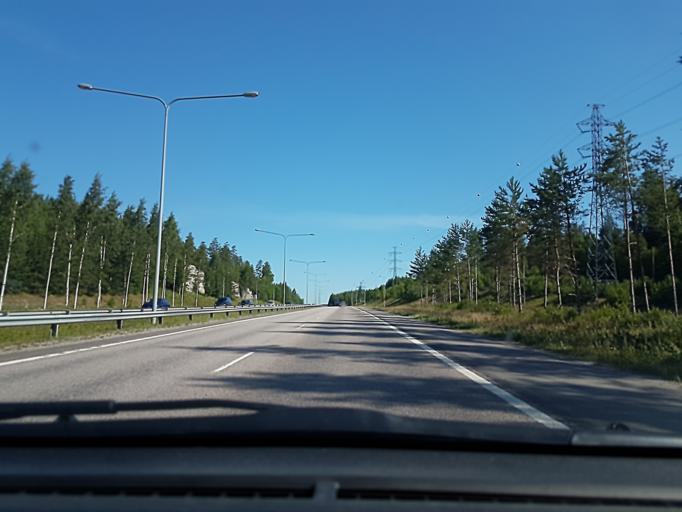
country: FI
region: Uusimaa
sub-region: Helsinki
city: Vantaa
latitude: 60.3248
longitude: 24.9980
